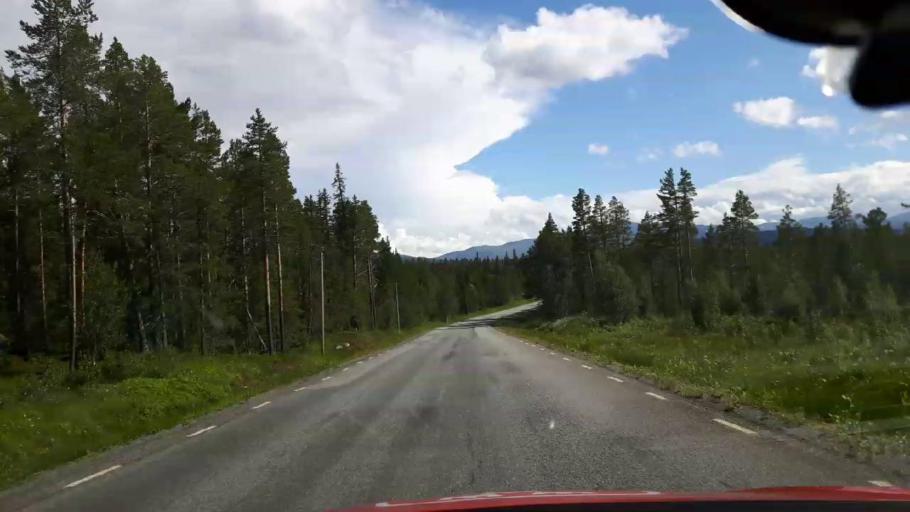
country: SE
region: Jaemtland
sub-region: Are Kommun
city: Are
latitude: 63.2232
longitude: 13.1630
